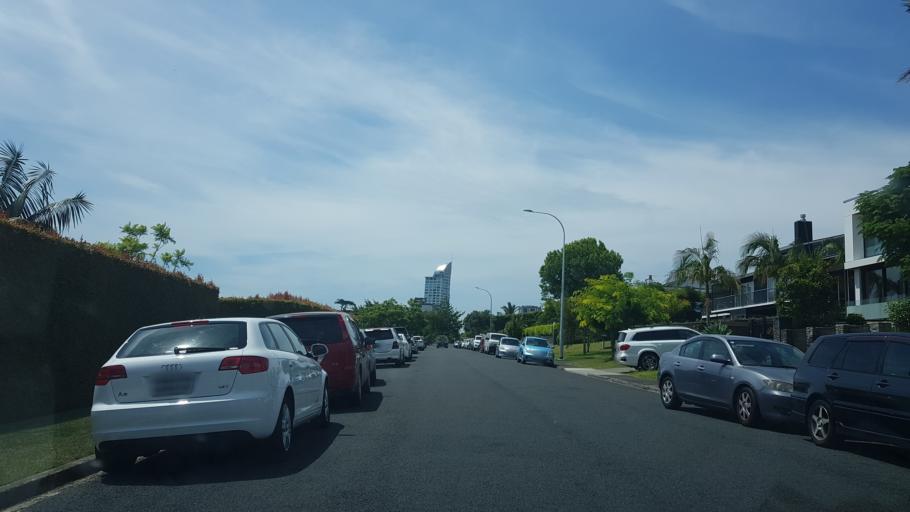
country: NZ
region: Auckland
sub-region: Auckland
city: North Shore
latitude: -36.7855
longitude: 174.7619
